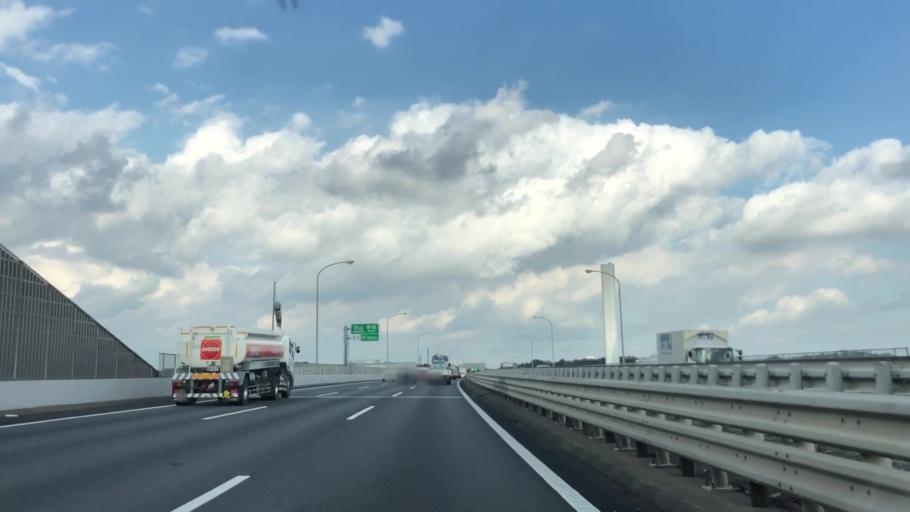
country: JP
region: Chiba
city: Nagareyama
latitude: 35.8740
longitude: 139.8914
